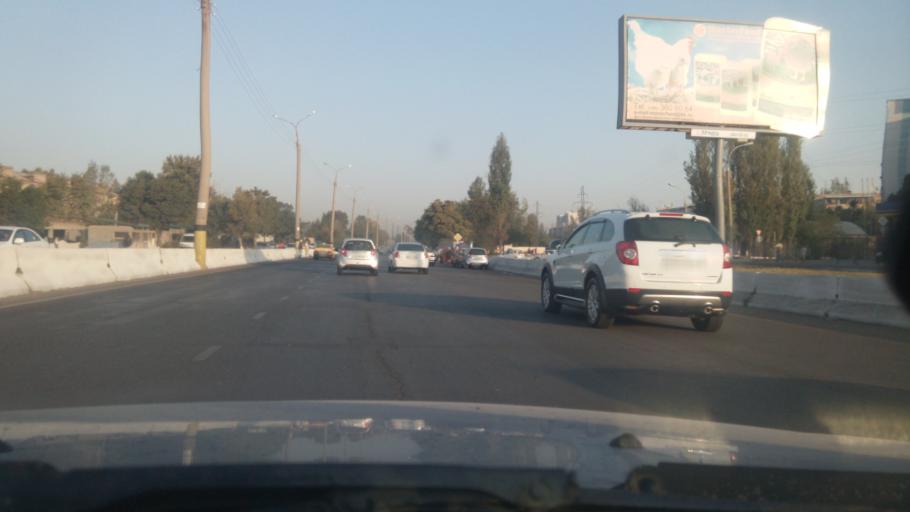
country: UZ
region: Toshkent Shahri
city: Tashkent
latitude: 41.2557
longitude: 69.1560
